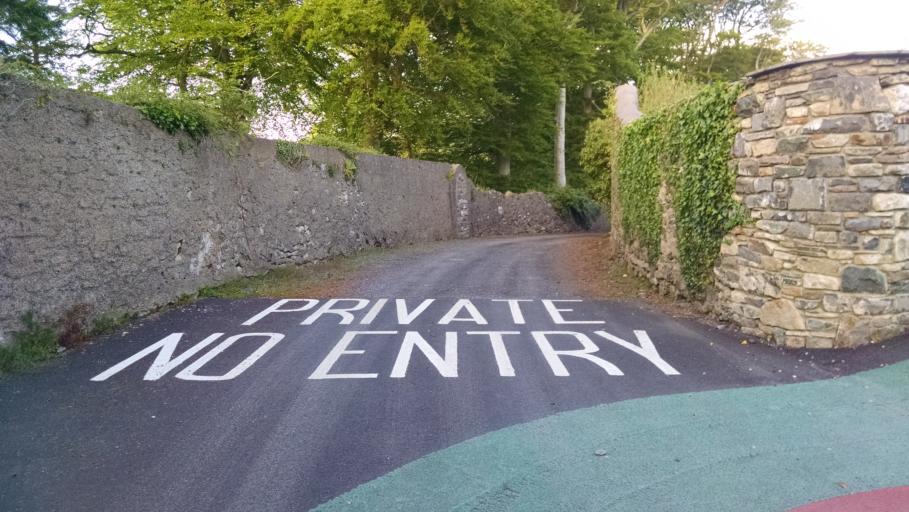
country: IE
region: Connaught
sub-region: Maigh Eo
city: Westport
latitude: 53.7998
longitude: -9.5151
